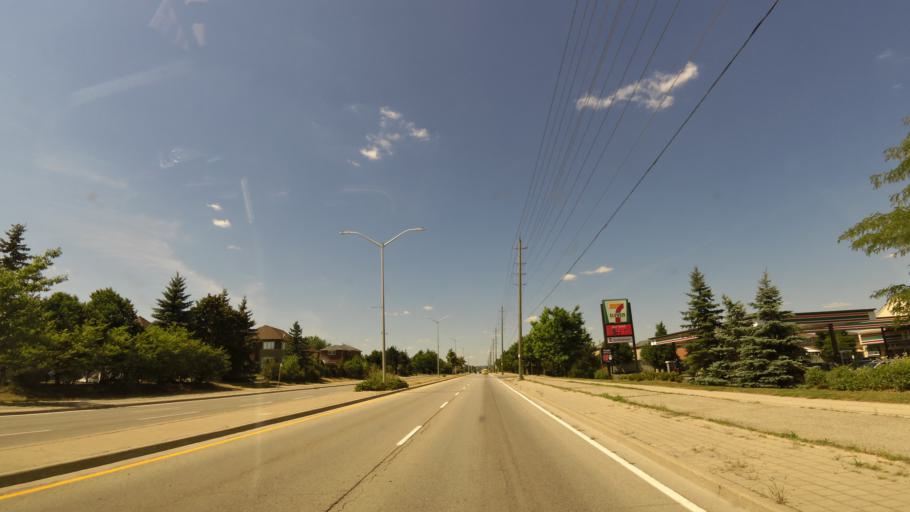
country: CA
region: Ontario
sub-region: Halton
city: Milton
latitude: 43.6324
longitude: -79.8793
